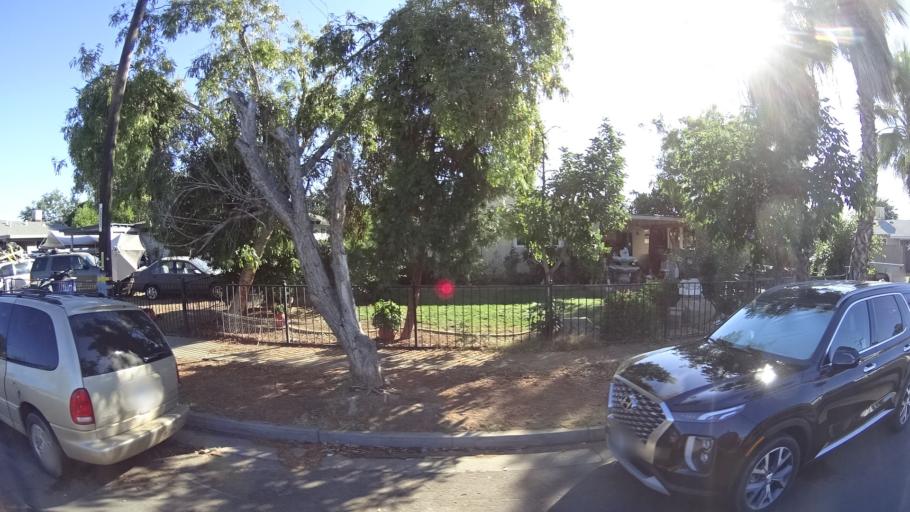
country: US
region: California
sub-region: Fresno County
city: Fresno
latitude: 36.7968
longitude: -119.8250
